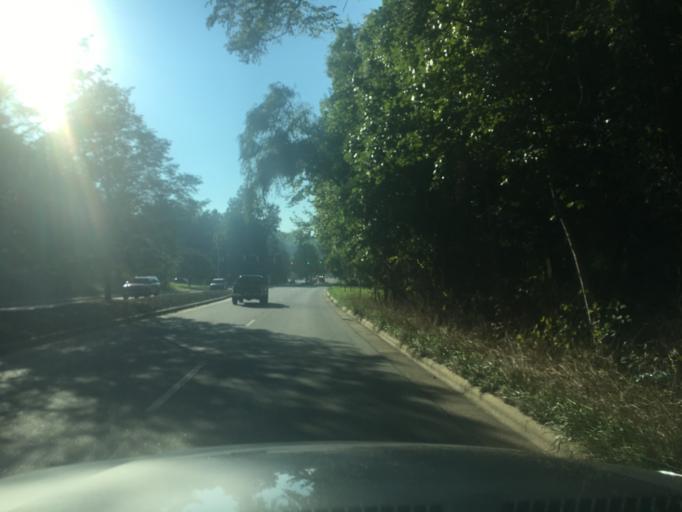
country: US
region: North Carolina
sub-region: Buncombe County
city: Asheville
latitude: 35.6131
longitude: -82.5694
